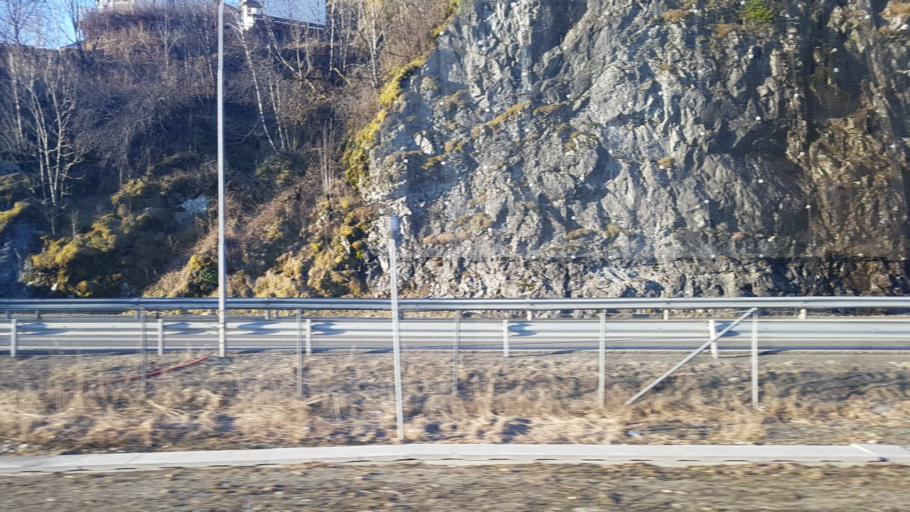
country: NO
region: Sor-Trondelag
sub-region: Malvik
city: Hommelvik
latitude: 63.4131
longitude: 10.7892
